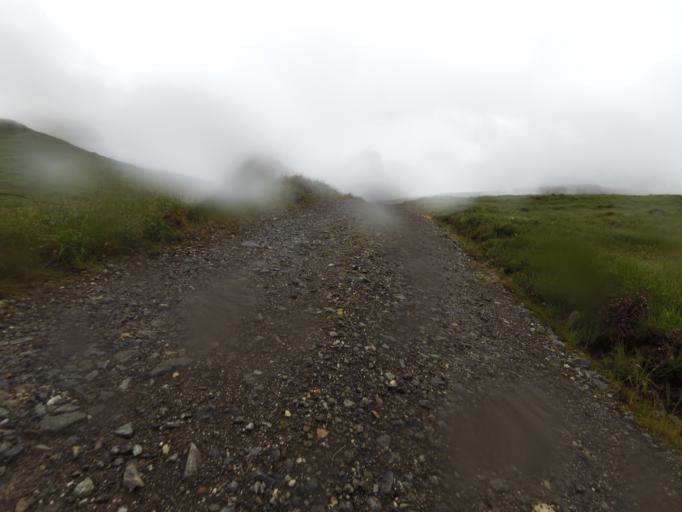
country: GB
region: Scotland
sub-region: Highland
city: Spean Bridge
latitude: 56.7697
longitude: -4.6952
